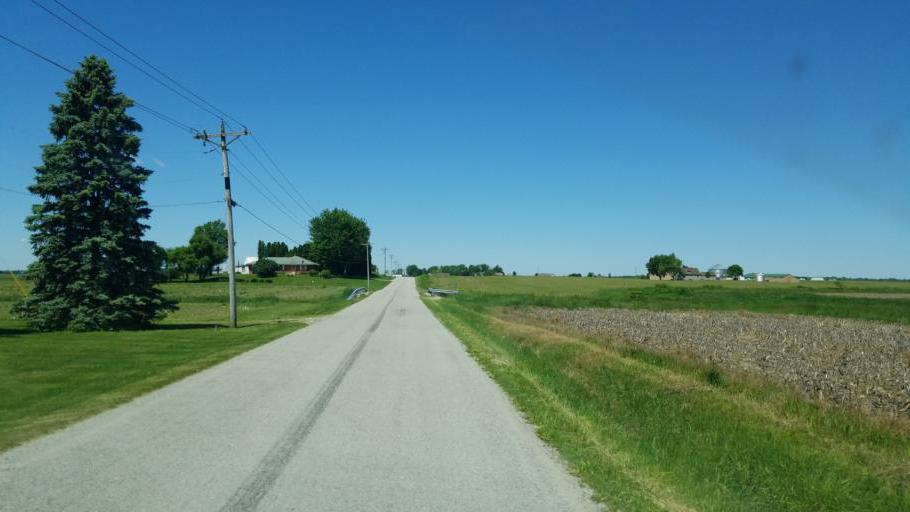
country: US
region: Ohio
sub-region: Shelby County
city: Anna
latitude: 40.3727
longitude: -84.2473
